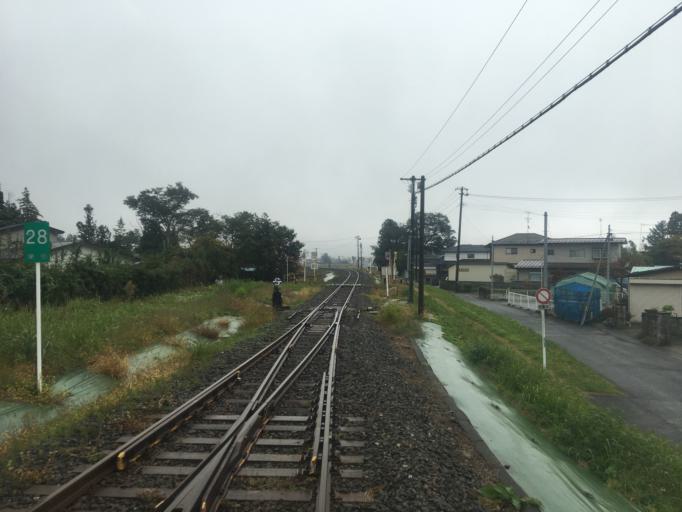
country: JP
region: Miyagi
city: Furukawa
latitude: 38.5767
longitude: 140.8968
